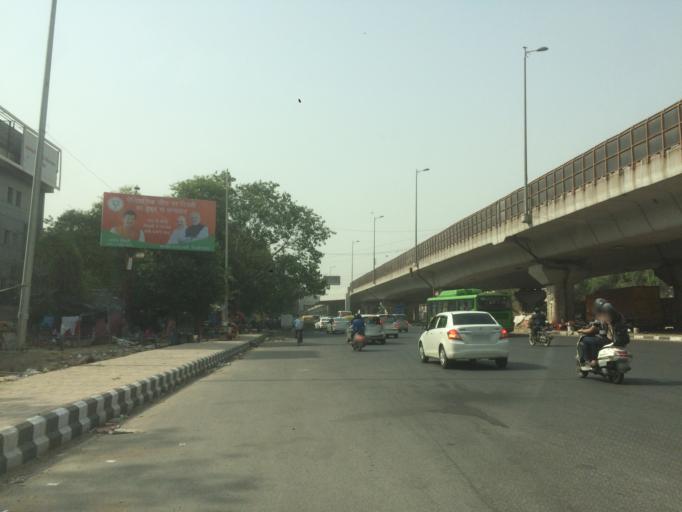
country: IN
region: NCT
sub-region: Central Delhi
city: Karol Bagh
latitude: 28.6274
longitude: 77.1342
